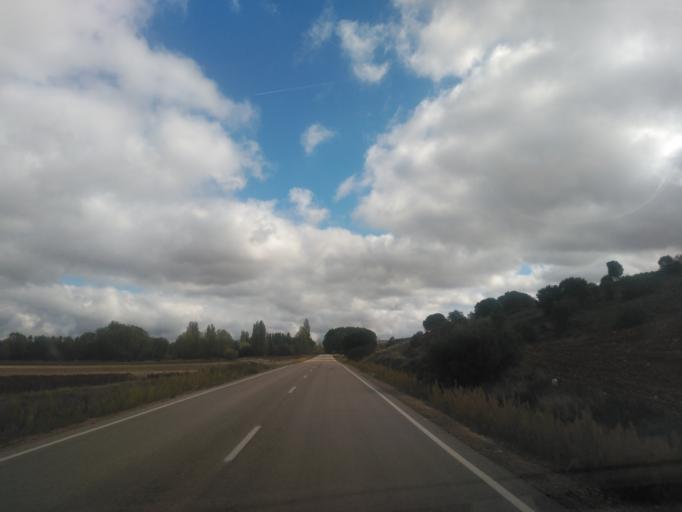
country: ES
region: Castille and Leon
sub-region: Provincia de Soria
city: Alcubilla de Avellaneda
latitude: 41.7535
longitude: -3.2744
